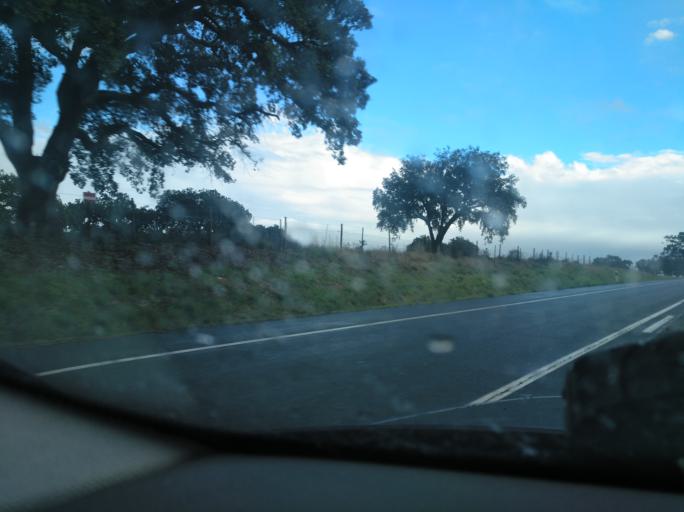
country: PT
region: Setubal
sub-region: Grandola
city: Grandola
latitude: 38.0193
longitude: -8.3981
